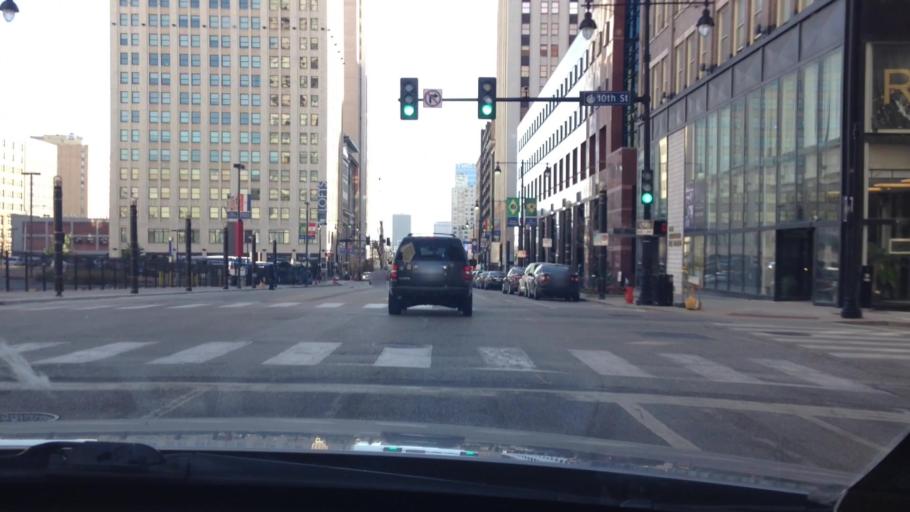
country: US
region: Missouri
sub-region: Jackson County
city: Kansas City
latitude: 39.1025
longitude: -94.5808
